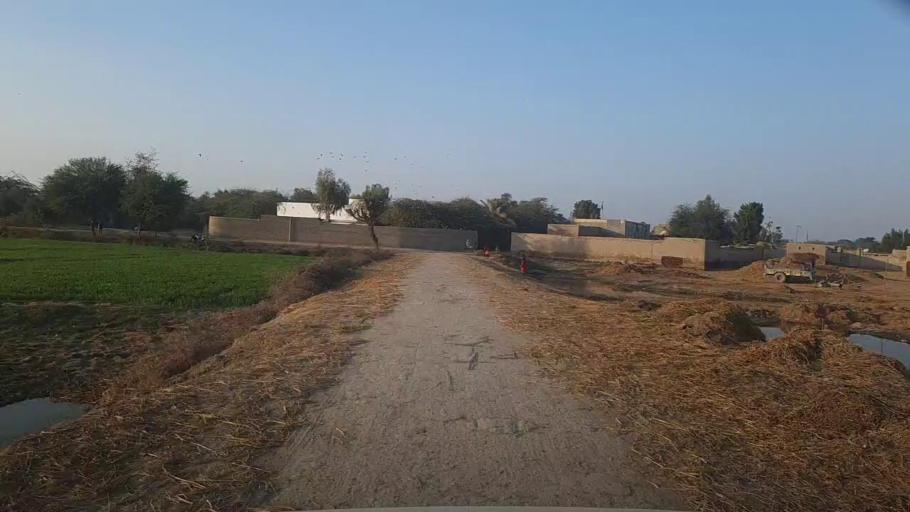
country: PK
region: Sindh
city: Mehar
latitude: 27.1979
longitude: 67.7812
